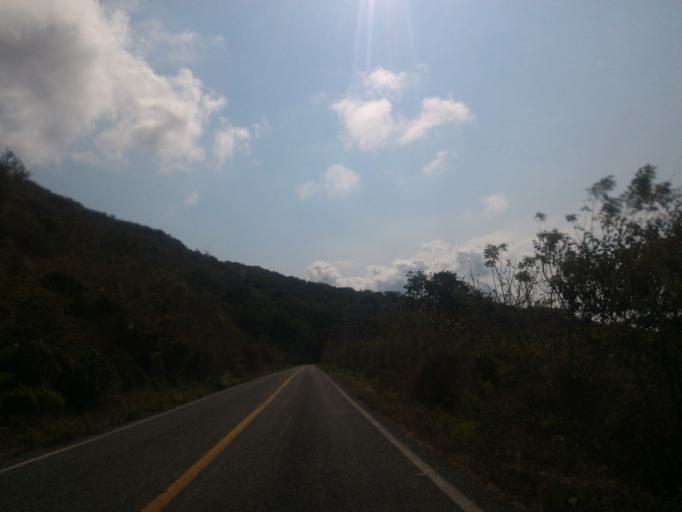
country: MX
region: Michoacan
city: Coahuayana Viejo
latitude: 18.4852
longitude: -103.5692
